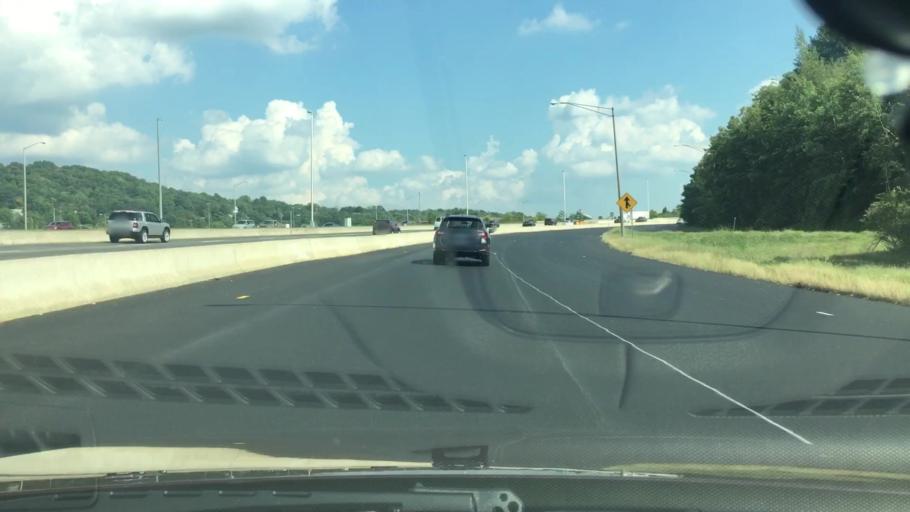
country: US
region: Connecticut
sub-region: New Haven County
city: Waterbury
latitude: 41.5531
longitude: -73.0314
